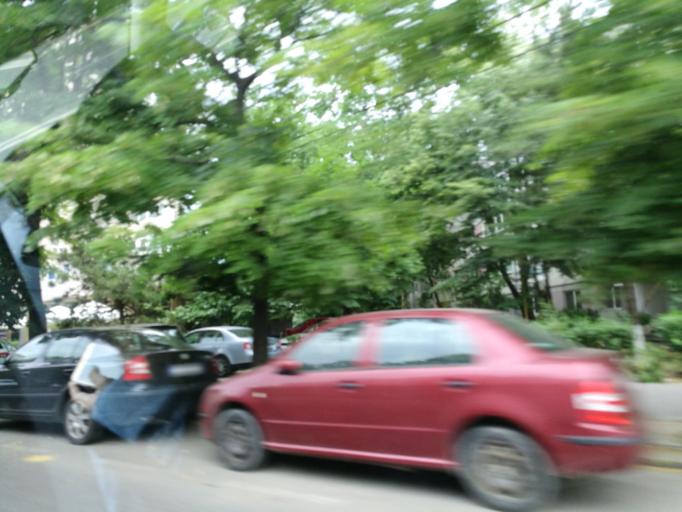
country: RO
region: Constanta
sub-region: Municipiul Constanta
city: Constanta
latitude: 44.1762
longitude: 28.6362
